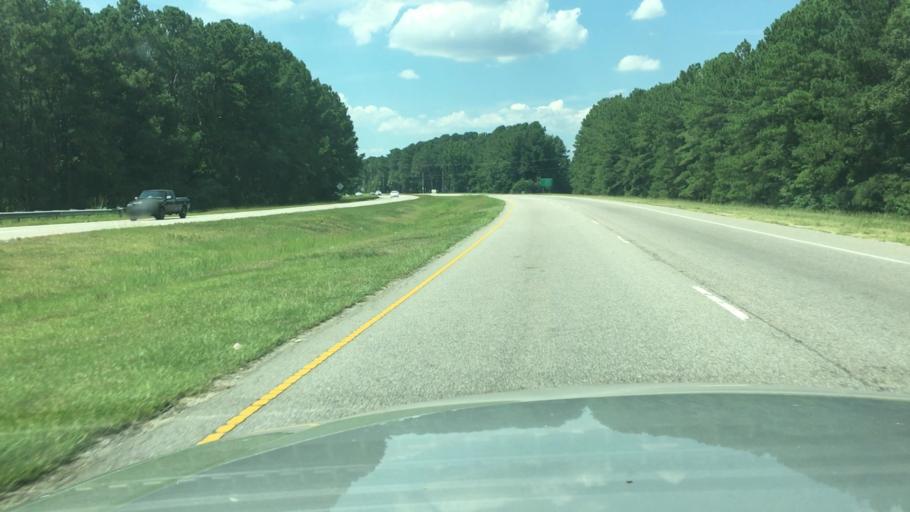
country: US
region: North Carolina
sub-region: Cumberland County
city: Vander
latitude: 34.9576
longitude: -78.8445
